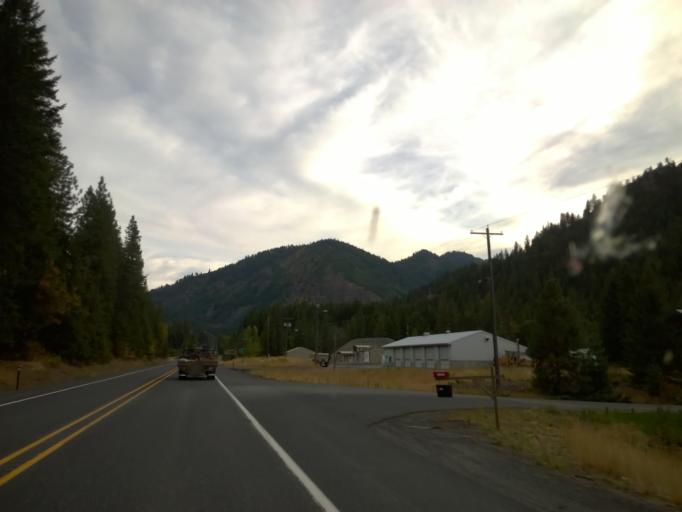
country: US
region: Washington
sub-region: Chelan County
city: Leavenworth
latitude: 47.4778
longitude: -120.6545
